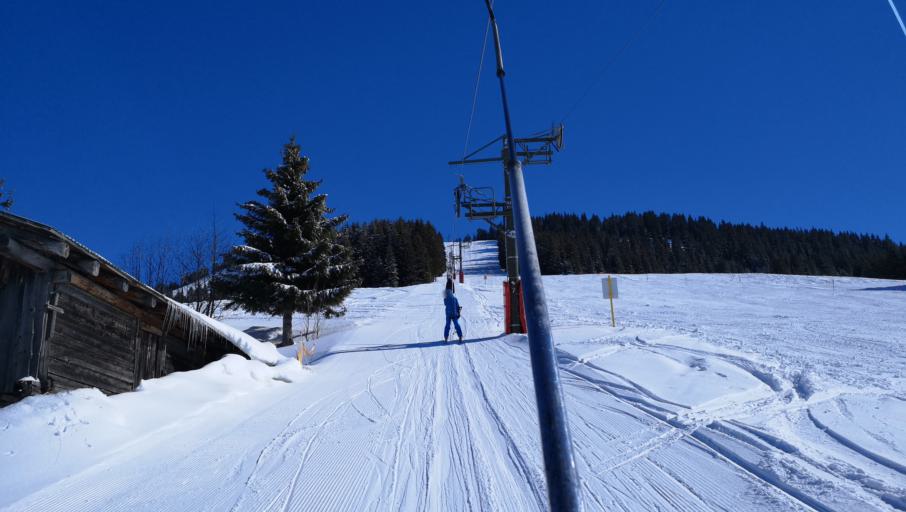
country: FR
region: Rhone-Alpes
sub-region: Departement de la Haute-Savoie
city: Megeve
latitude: 45.8440
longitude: 6.6569
